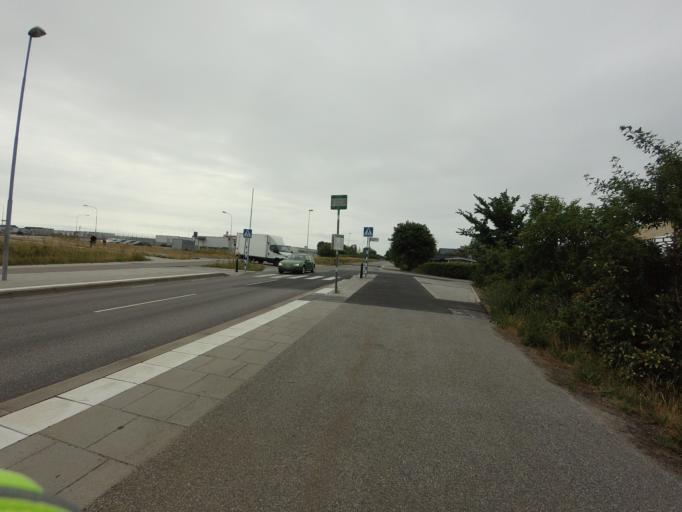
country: SE
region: Skane
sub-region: Malmo
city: Bunkeflostrand
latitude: 55.5408
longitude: 12.9191
